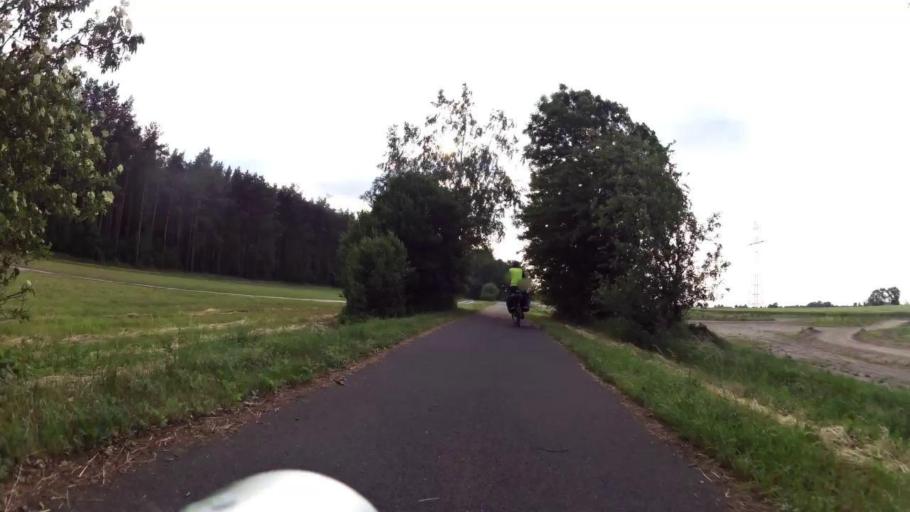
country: PL
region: Kujawsko-Pomorskie
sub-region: Powiat chelminski
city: Unislaw
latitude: 53.1846
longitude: 18.3862
